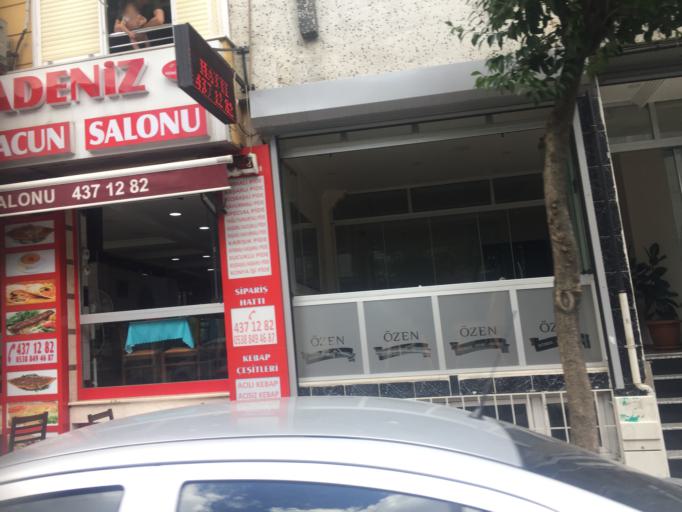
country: TR
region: Istanbul
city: Esenler
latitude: 41.0537
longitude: 28.9000
